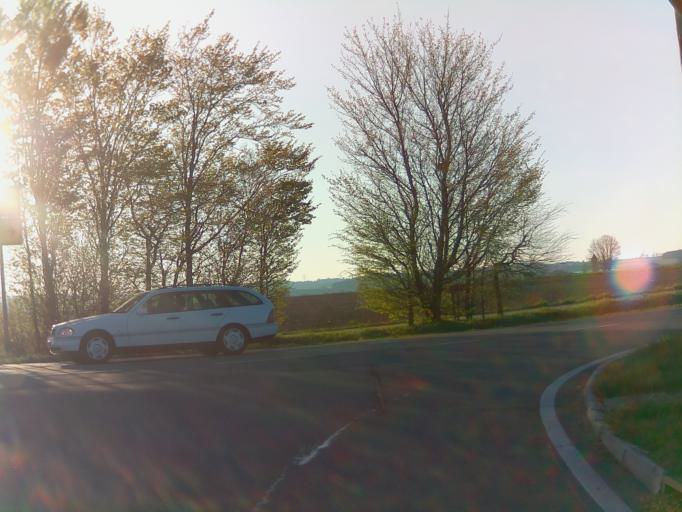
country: DE
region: Baden-Wuerttemberg
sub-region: Regierungsbezirk Stuttgart
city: Kupferzell
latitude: 49.2146
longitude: 9.6770
